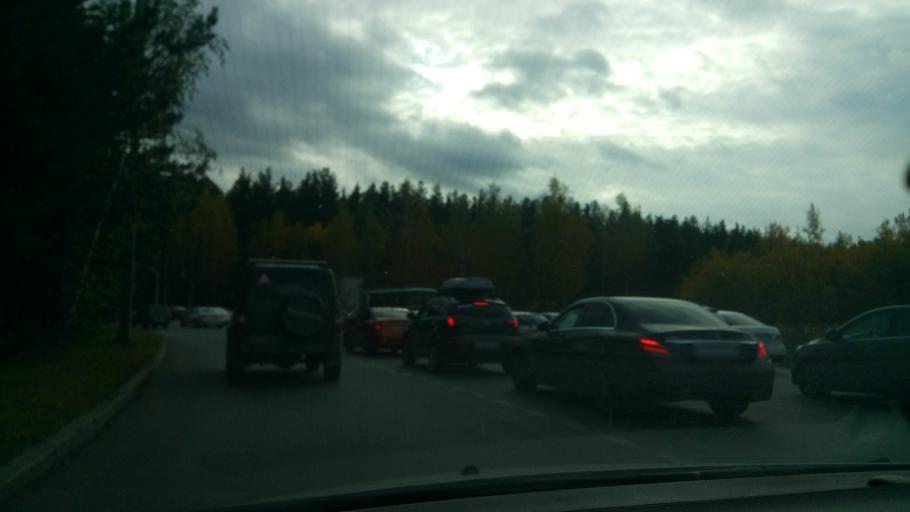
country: RU
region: Sverdlovsk
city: Sovkhoznyy
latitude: 56.8052
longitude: 60.5379
